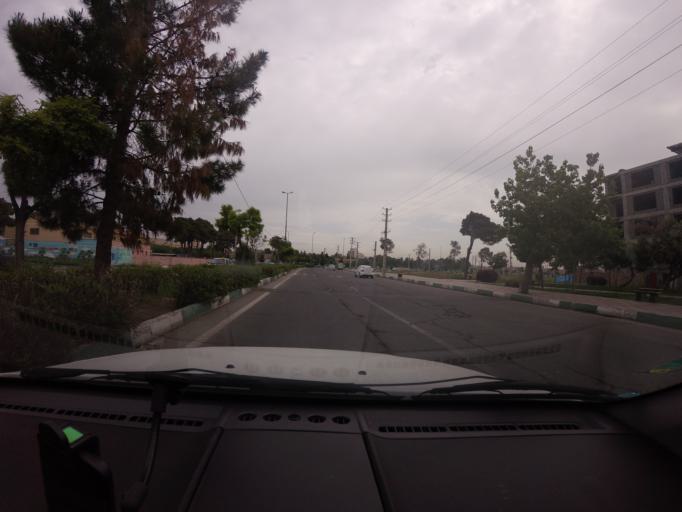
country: IR
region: Tehran
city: Eslamshahr
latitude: 35.5379
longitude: 51.2220
